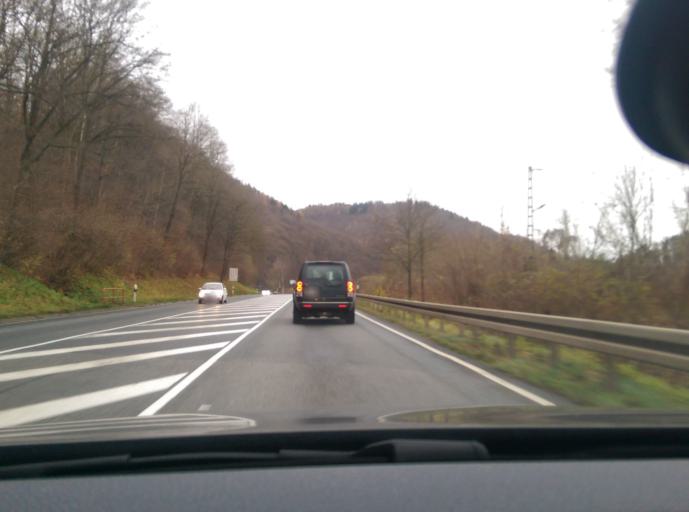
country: DE
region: Hesse
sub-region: Regierungsbezirk Kassel
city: Bad Sooden-Allendorf
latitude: 51.2343
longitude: 9.9878
